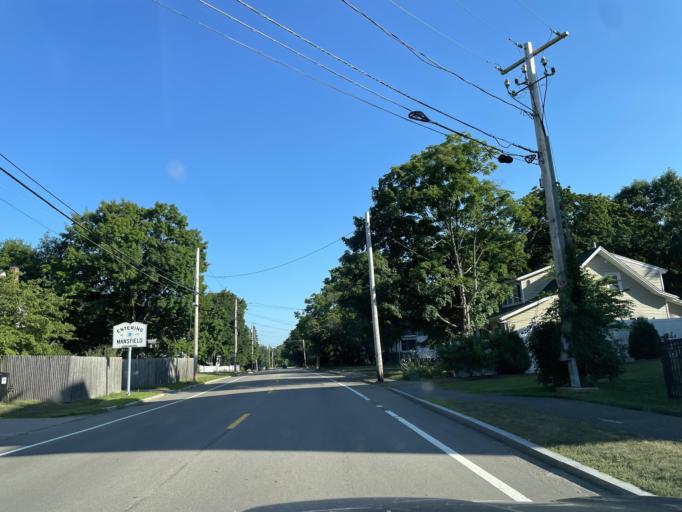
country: US
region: Massachusetts
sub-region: Bristol County
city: Mansfield
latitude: 42.0369
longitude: -71.2319
